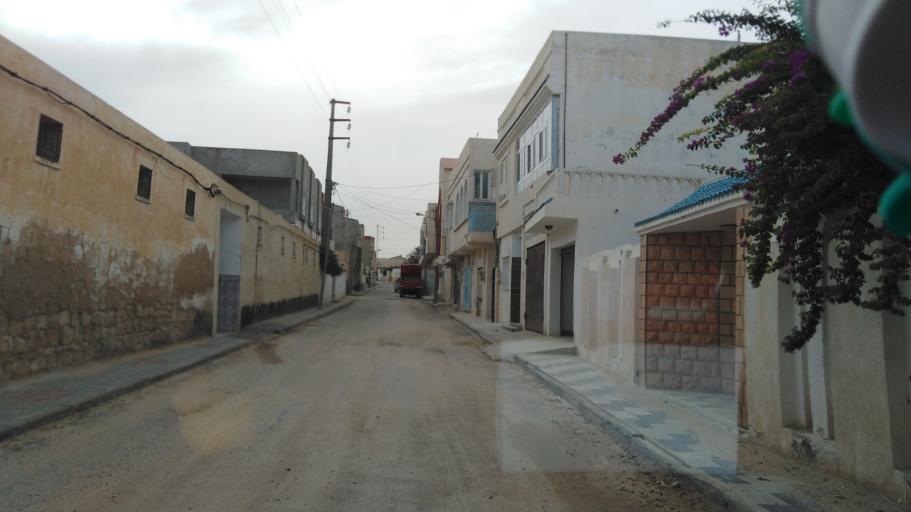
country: TN
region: Qabis
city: Gabes
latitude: 33.9572
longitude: 10.0047
